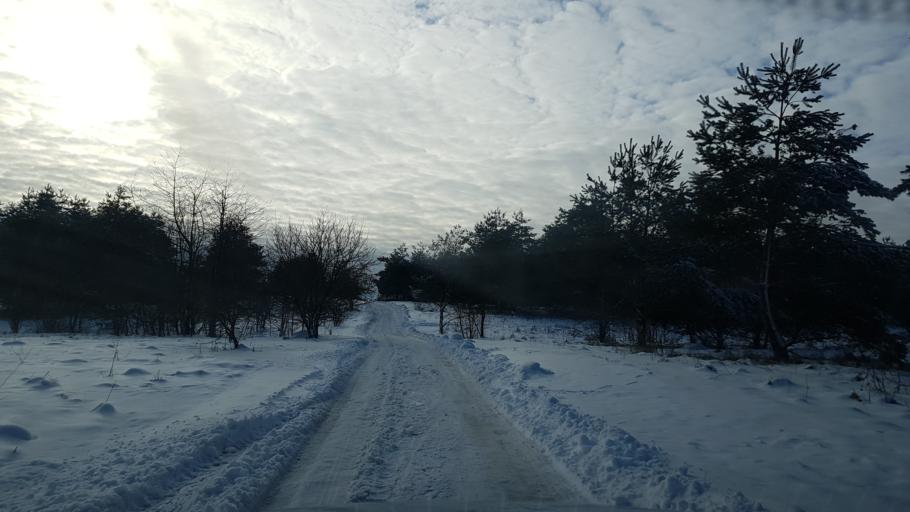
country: PL
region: West Pomeranian Voivodeship
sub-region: Powiat drawski
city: Drawsko Pomorskie
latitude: 53.5455
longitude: 15.8065
